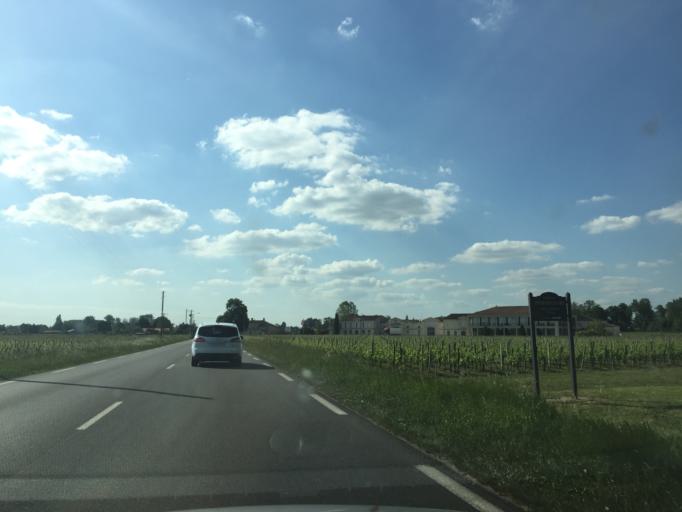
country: FR
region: Aquitaine
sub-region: Departement de la Gironde
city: Saint-Sulpice-de-Faleyrens
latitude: 44.8861
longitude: -0.1819
